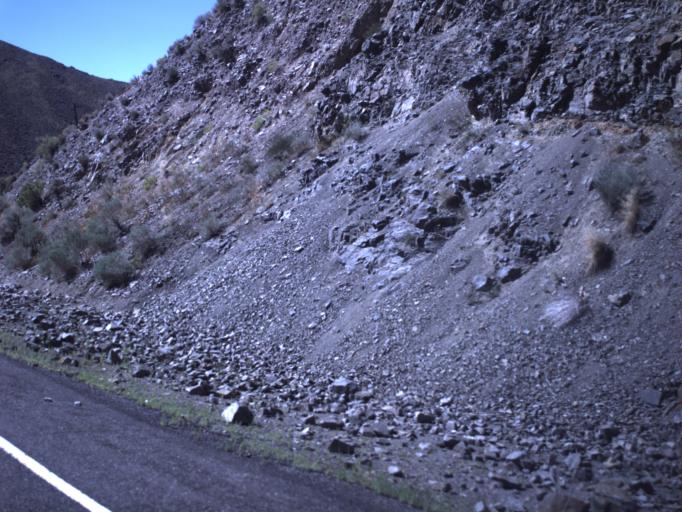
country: US
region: Utah
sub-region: Sevier County
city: Monroe
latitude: 38.4903
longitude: -112.2434
